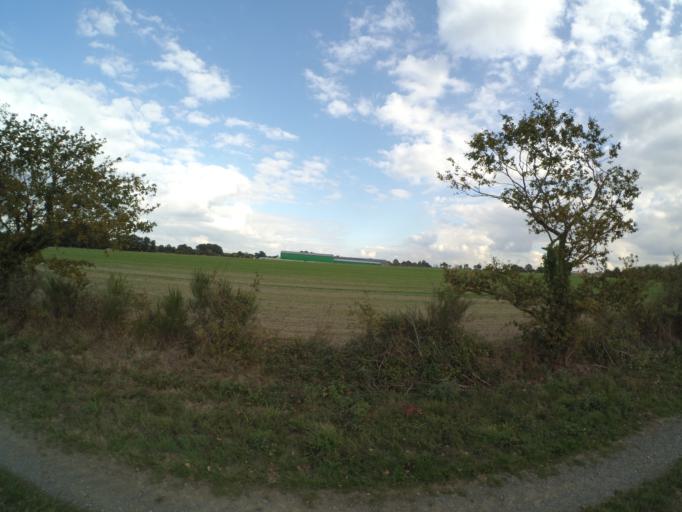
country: FR
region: Pays de la Loire
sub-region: Departement de la Loire-Atlantique
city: Saint-Lumine-de-Clisson
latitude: 47.0748
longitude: -1.3336
